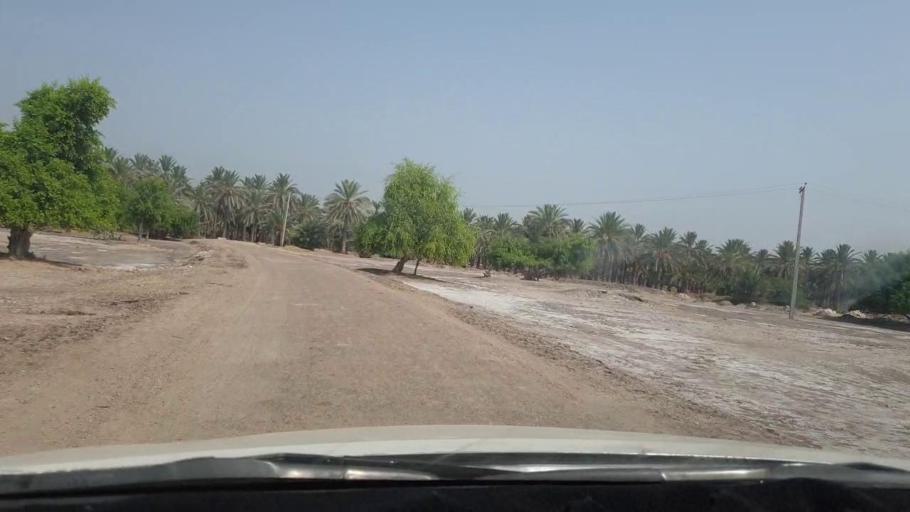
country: PK
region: Sindh
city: Rohri
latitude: 27.6256
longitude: 68.8880
